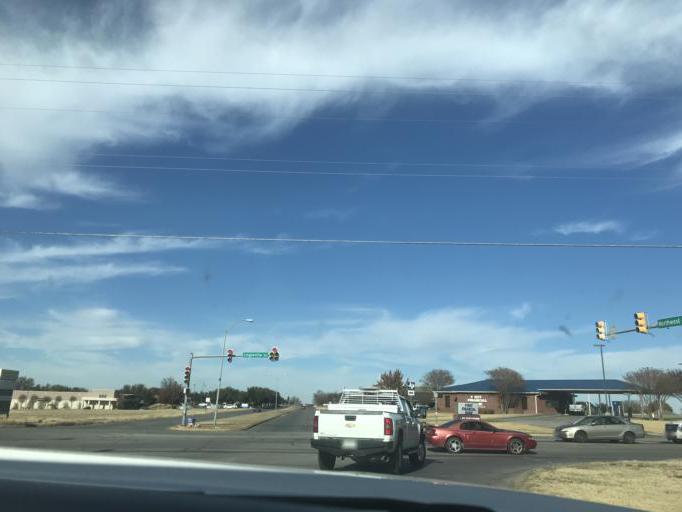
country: US
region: Texas
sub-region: Erath County
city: Stephenville
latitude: 32.2258
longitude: -98.2324
